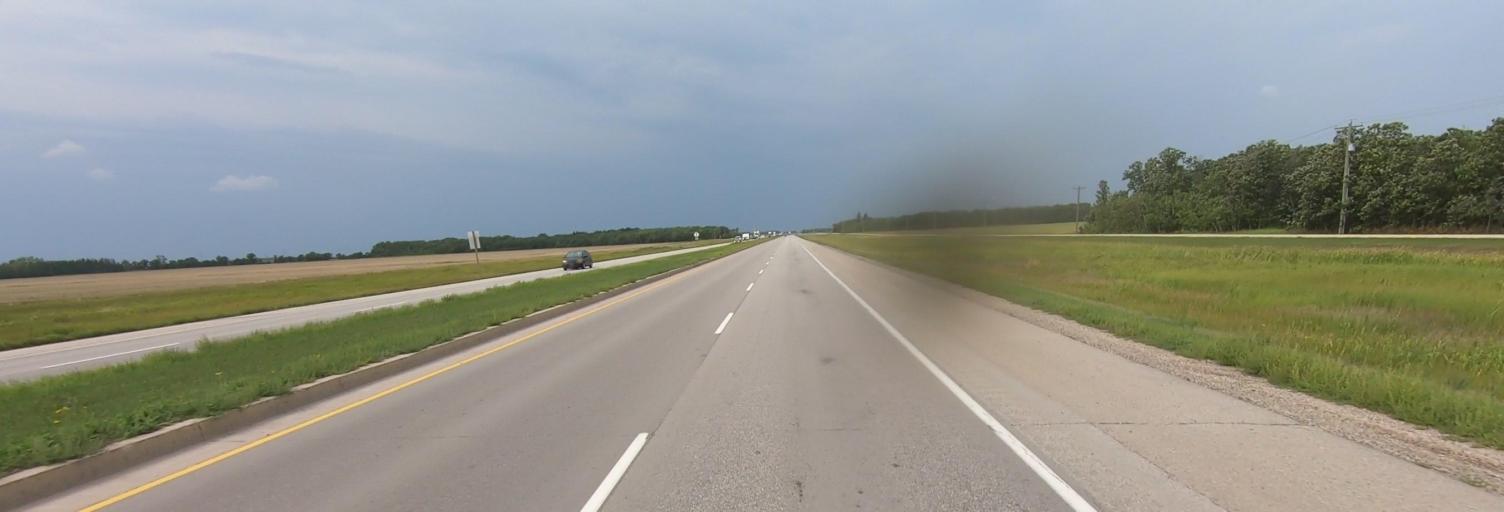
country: CA
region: Manitoba
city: Winnipeg
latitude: 49.7682
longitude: -97.2425
